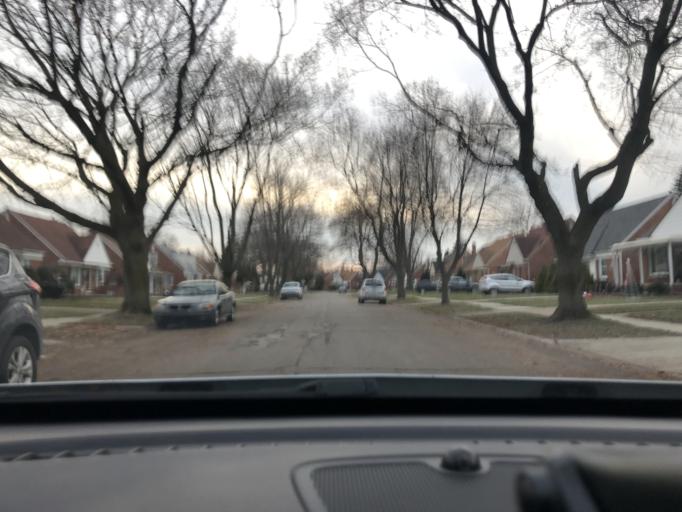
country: US
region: Michigan
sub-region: Wayne County
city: Allen Park
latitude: 42.2862
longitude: -83.2204
